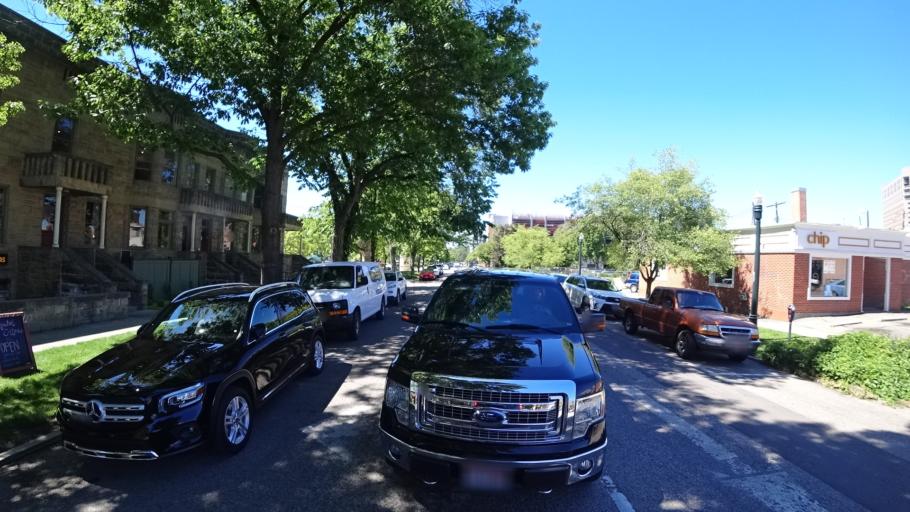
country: US
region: Idaho
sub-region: Ada County
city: Boise
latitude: 43.6136
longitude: -116.2001
